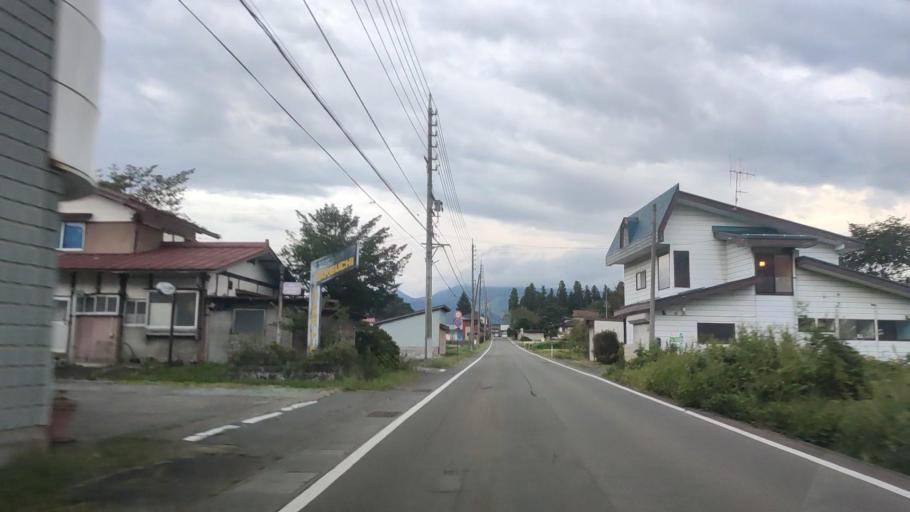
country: JP
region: Nagano
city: Iiyama
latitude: 36.8709
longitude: 138.4076
